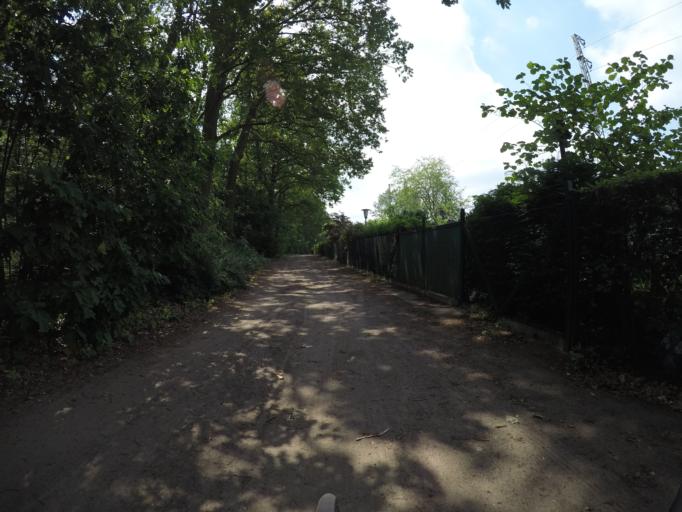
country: DE
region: Berlin
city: Grunewald
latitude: 52.4782
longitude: 13.2511
